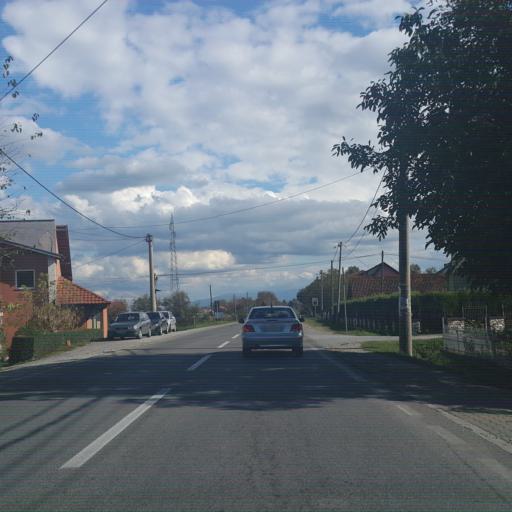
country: RS
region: Central Serbia
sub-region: Rasinski Okrug
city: Trstenik
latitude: 43.5968
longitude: 21.0588
